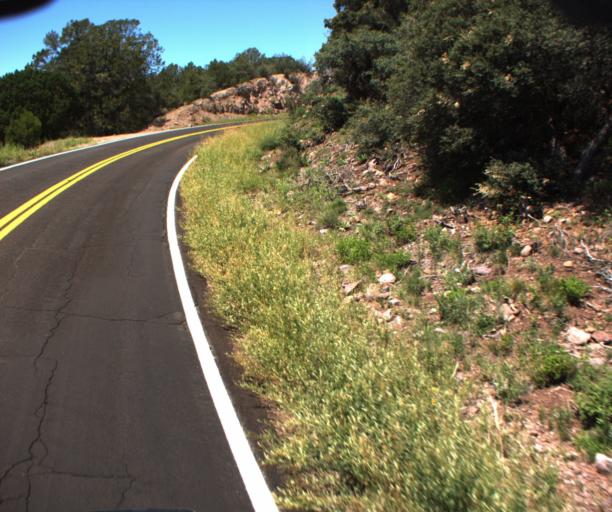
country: US
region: Arizona
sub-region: Greenlee County
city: Morenci
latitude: 33.4280
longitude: -109.3751
